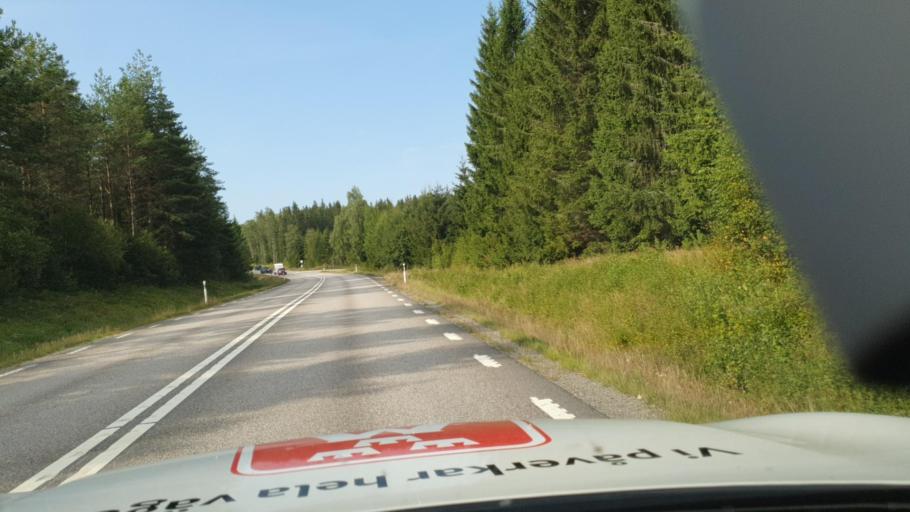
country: SE
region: Vaestra Goetaland
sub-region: Dals-Ed Kommun
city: Ed
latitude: 58.8759
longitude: 11.7819
